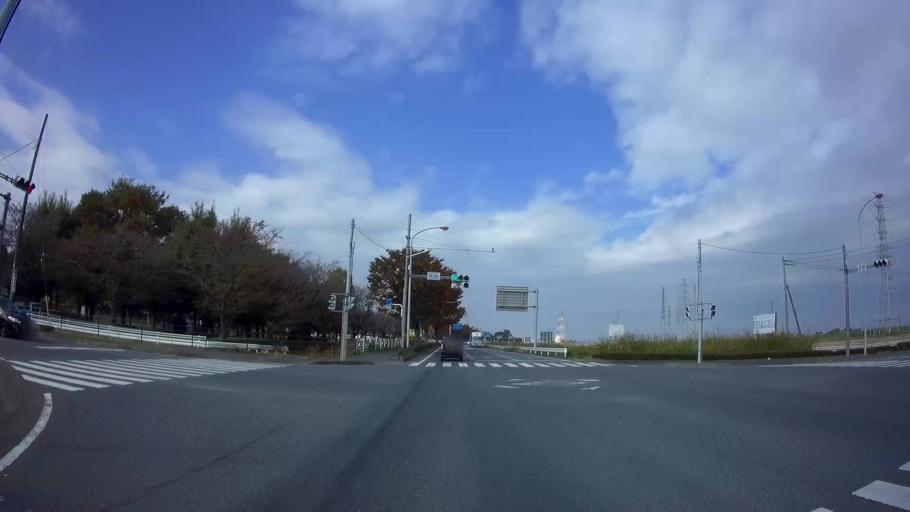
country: JP
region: Saitama
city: Fukayacho
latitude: 36.2194
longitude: 139.2407
